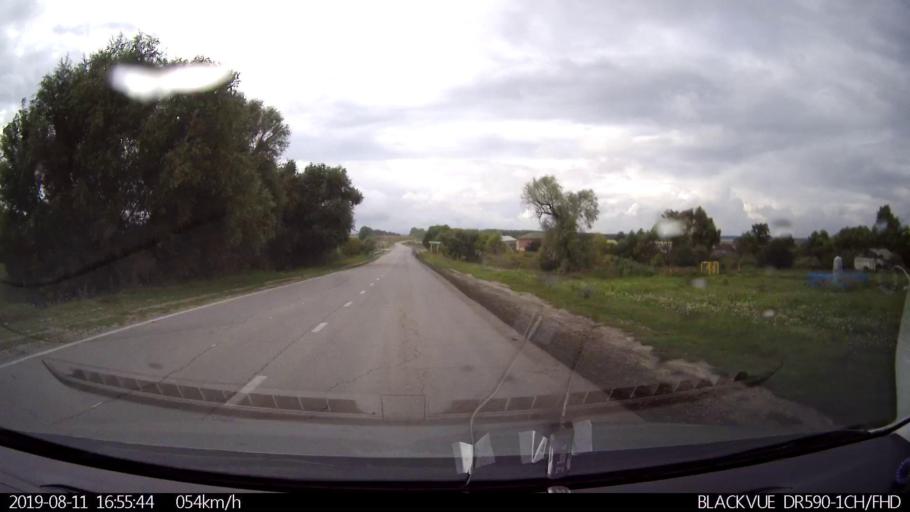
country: RU
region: Ulyanovsk
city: Mayna
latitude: 54.2836
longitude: 47.6606
